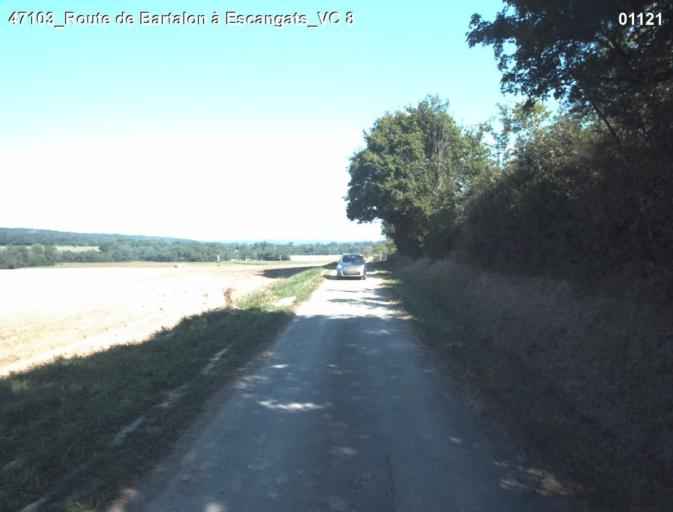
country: FR
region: Aquitaine
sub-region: Departement du Lot-et-Garonne
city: Nerac
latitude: 44.0859
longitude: 0.3166
